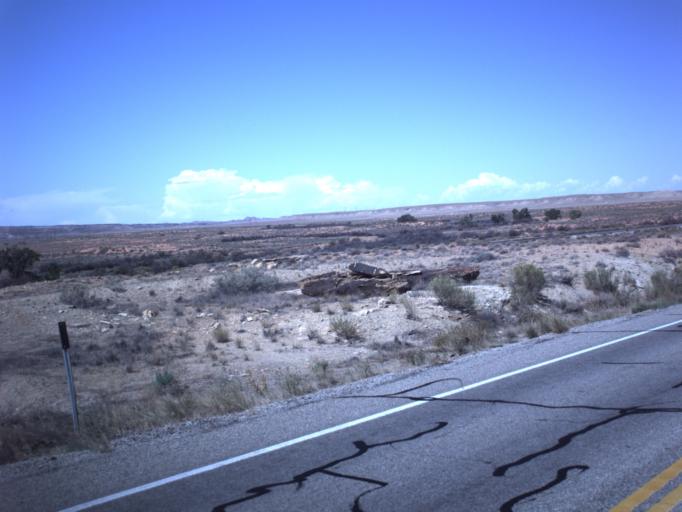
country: US
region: Utah
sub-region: Grand County
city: Moab
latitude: 38.7360
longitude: -109.7308
